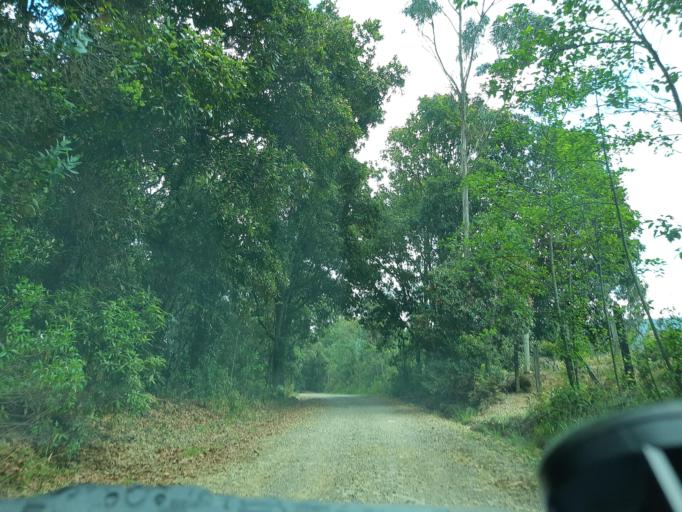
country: CO
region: Boyaca
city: Raquira
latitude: 5.5065
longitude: -73.6744
